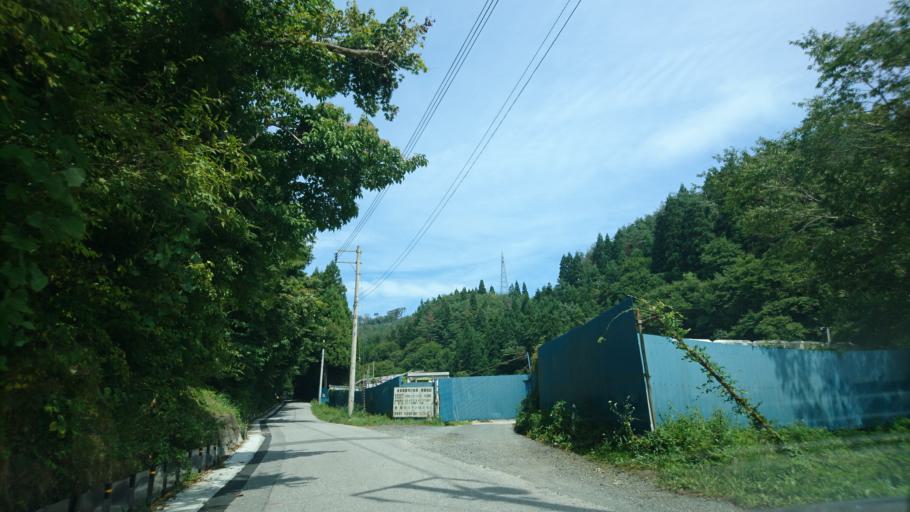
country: JP
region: Iwate
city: Ofunato
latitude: 38.9293
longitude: 141.5878
